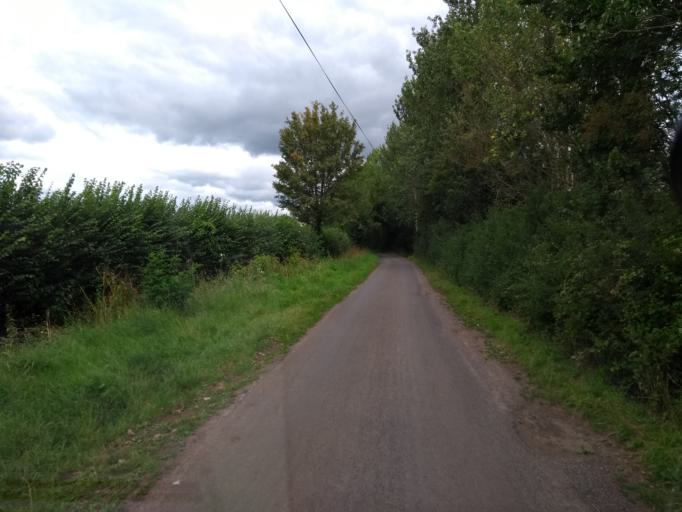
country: GB
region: England
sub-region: Somerset
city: Creech Saint Michael
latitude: 51.0367
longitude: -3.0148
